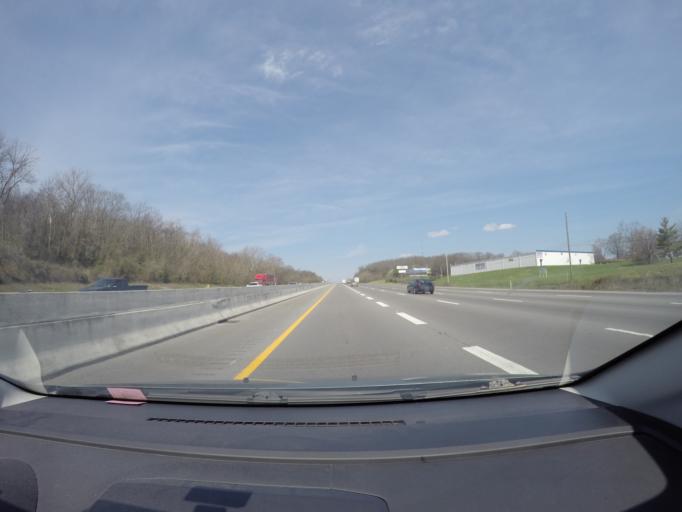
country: US
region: Tennessee
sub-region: Rutherford County
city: La Vergne
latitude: 36.0174
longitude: -86.6238
